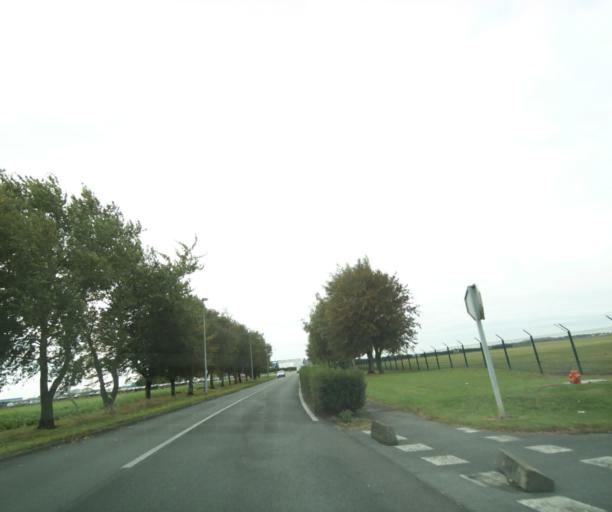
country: FR
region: Nord-Pas-de-Calais
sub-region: Departement du Nord
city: Vendeville
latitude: 50.5728
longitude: 3.0967
